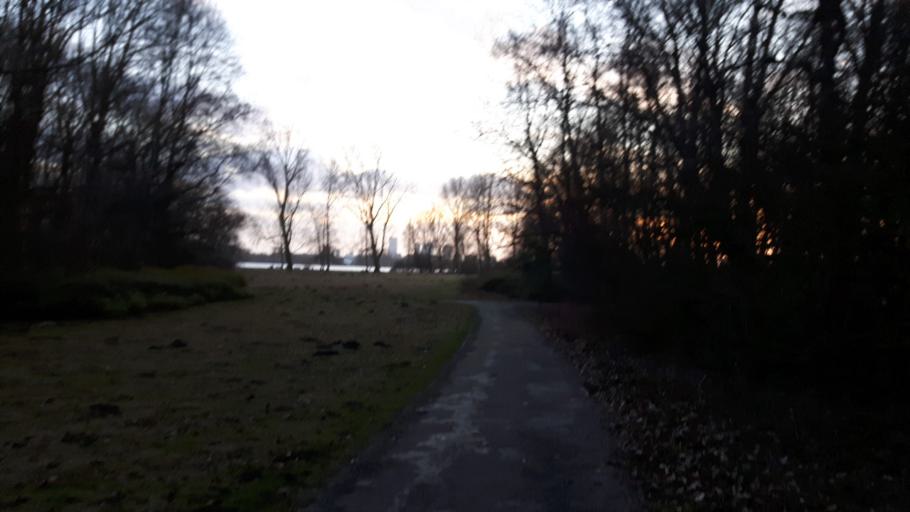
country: NL
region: South Holland
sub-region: Gemeente Rotterdam
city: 's-Gravenland
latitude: 51.9424
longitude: 4.5203
